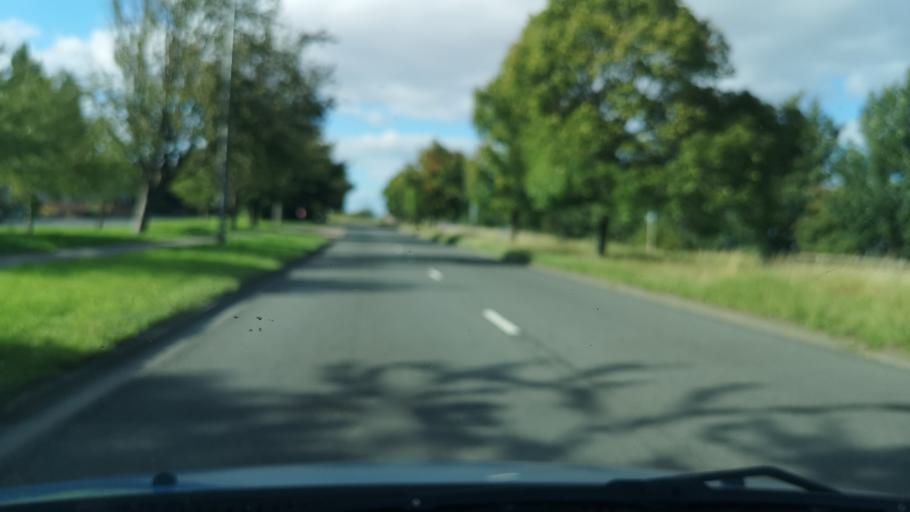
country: GB
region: England
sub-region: Doncaster
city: Carcroft
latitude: 53.5721
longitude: -1.2015
